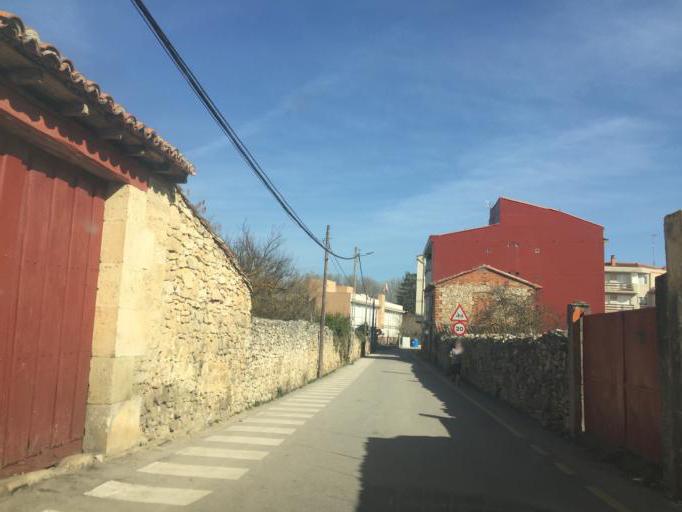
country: ES
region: Castille and Leon
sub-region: Provincia de Burgos
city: Medina de Pomar
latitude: 42.9385
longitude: -3.5754
